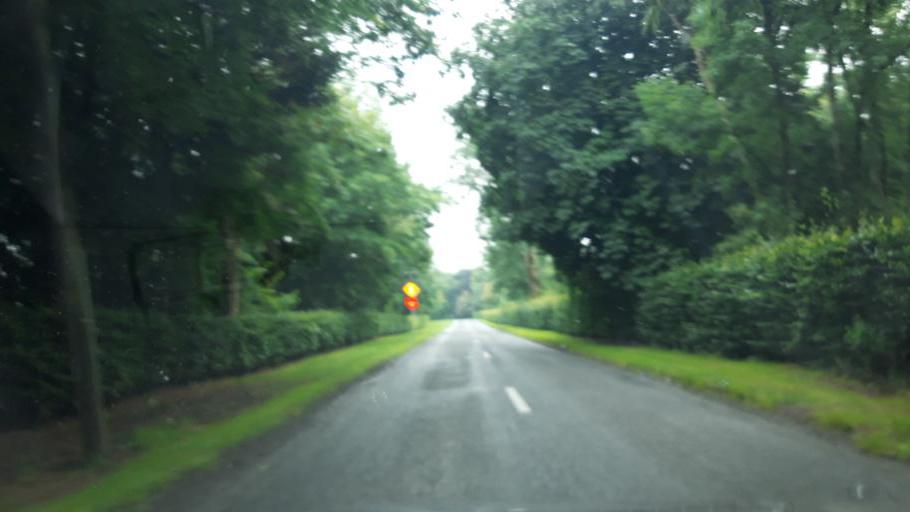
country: IE
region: Munster
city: Fethard
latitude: 52.5092
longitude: -7.6856
